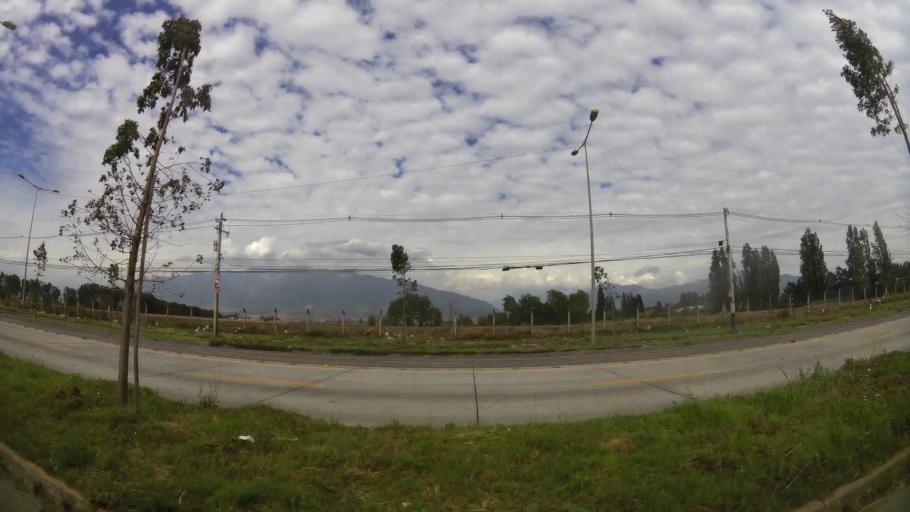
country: CL
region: Santiago Metropolitan
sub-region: Provincia de Santiago
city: La Pintana
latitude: -33.5808
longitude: -70.6292
